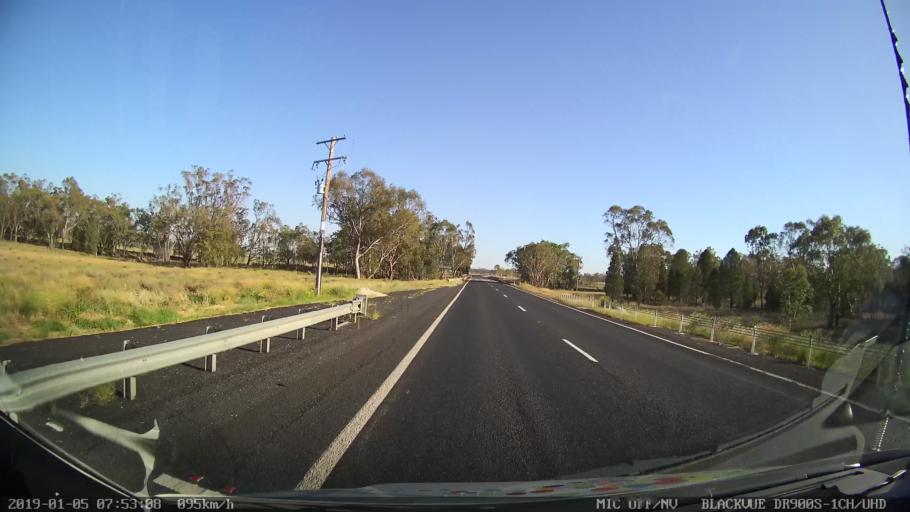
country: AU
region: New South Wales
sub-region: Gilgandra
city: Gilgandra
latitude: -31.7486
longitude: 148.6410
